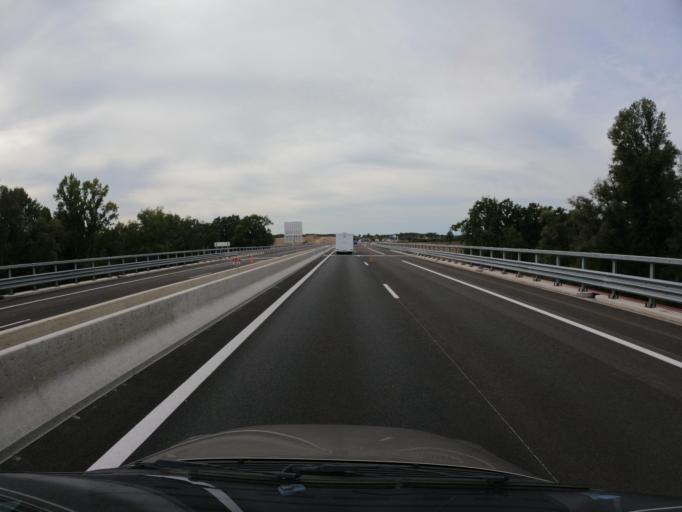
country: FR
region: Auvergne
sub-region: Departement de l'Allier
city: Bessay-sur-Allier
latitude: 46.4787
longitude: 3.3262
